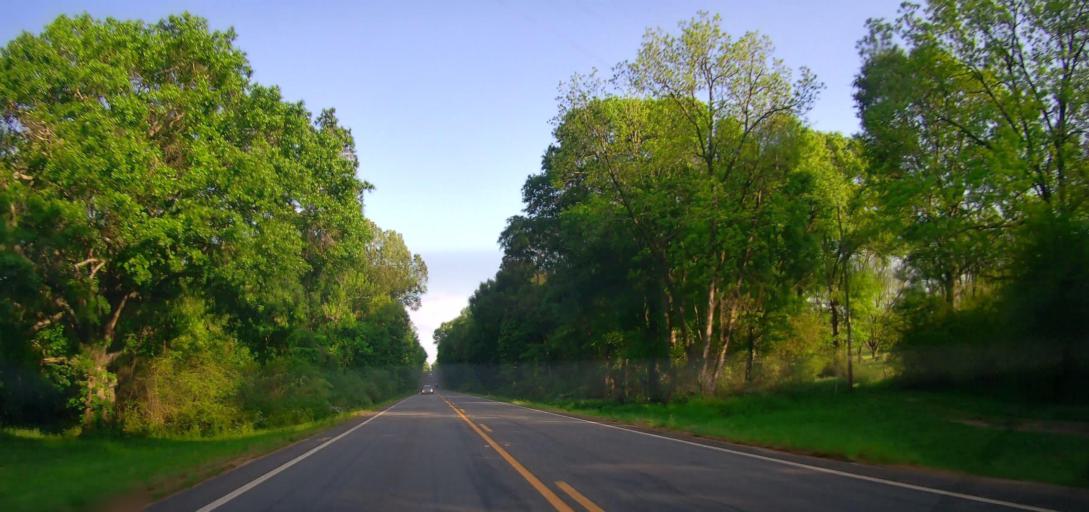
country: US
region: Georgia
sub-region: Putnam County
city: Eatonton
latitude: 33.3694
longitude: -83.5310
